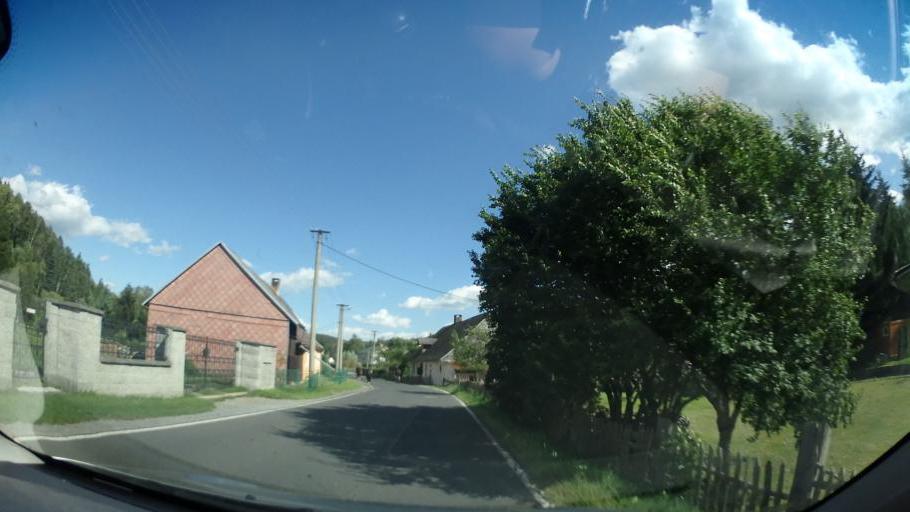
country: CZ
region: Olomoucky
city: Vapenna
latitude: 50.2225
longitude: 17.1002
